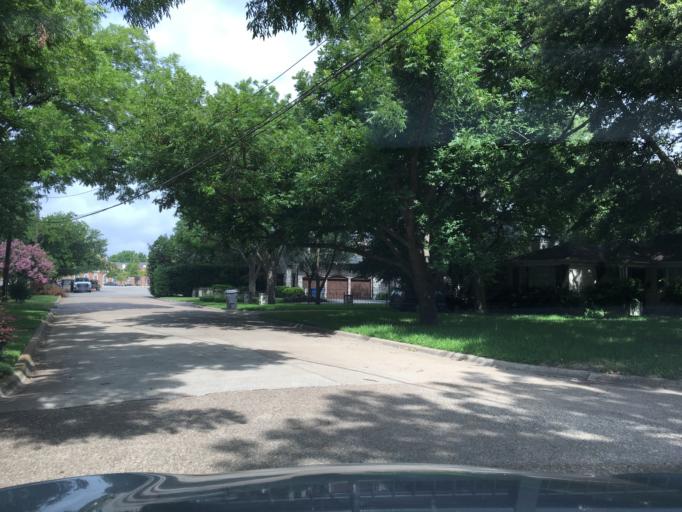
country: US
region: Texas
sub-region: Dallas County
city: University Park
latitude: 32.8812
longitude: -96.7999
